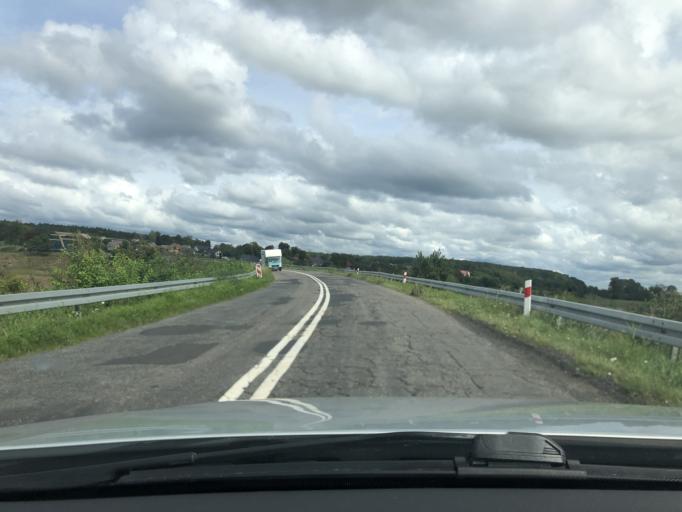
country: PL
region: Lubusz
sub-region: Powiat strzelecko-drezdenecki
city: Drezdenko
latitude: 52.8430
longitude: 15.9161
